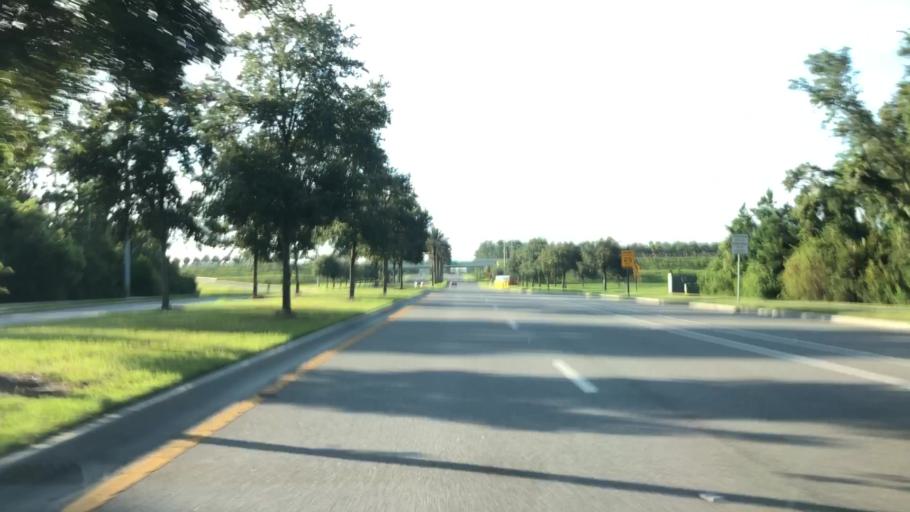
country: US
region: Florida
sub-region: Saint Johns County
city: Palm Valley
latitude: 30.1140
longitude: -81.4489
